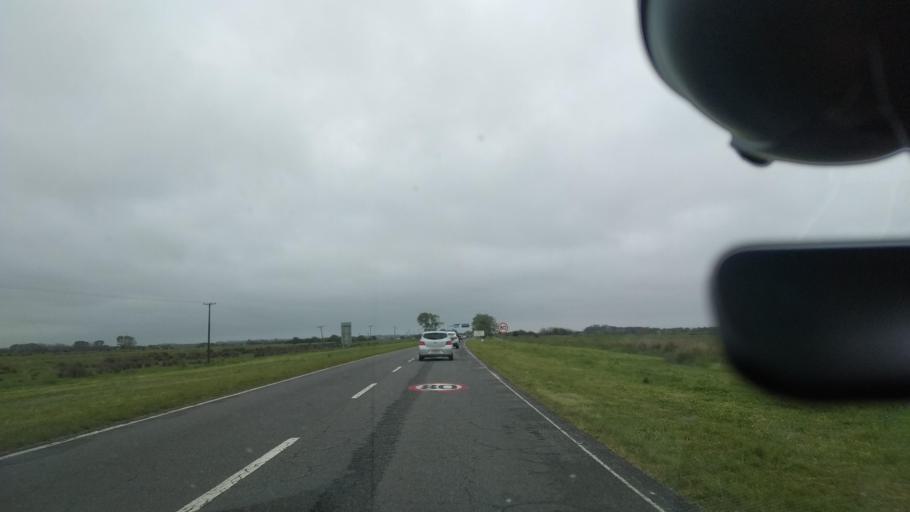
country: AR
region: Buenos Aires
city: Veronica
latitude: -35.5980
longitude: -57.2729
